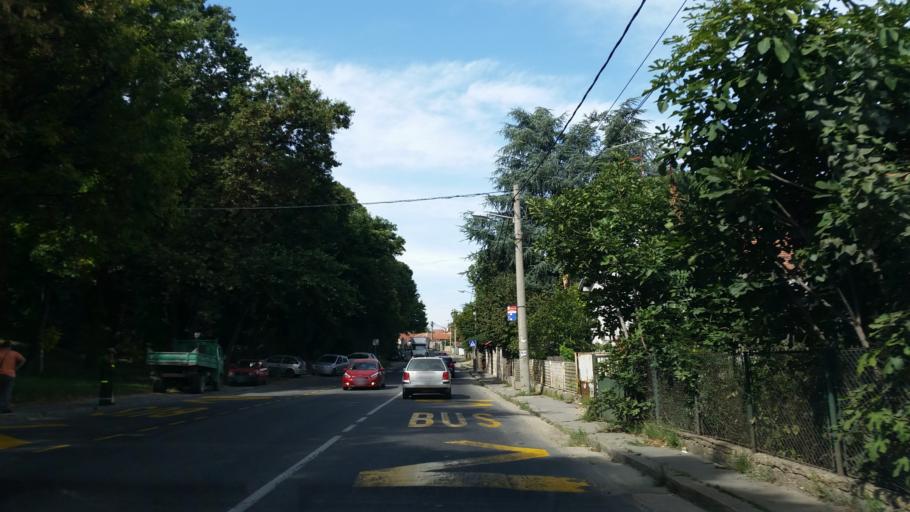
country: RS
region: Central Serbia
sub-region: Belgrade
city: Palilula
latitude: 44.8117
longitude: 20.5073
